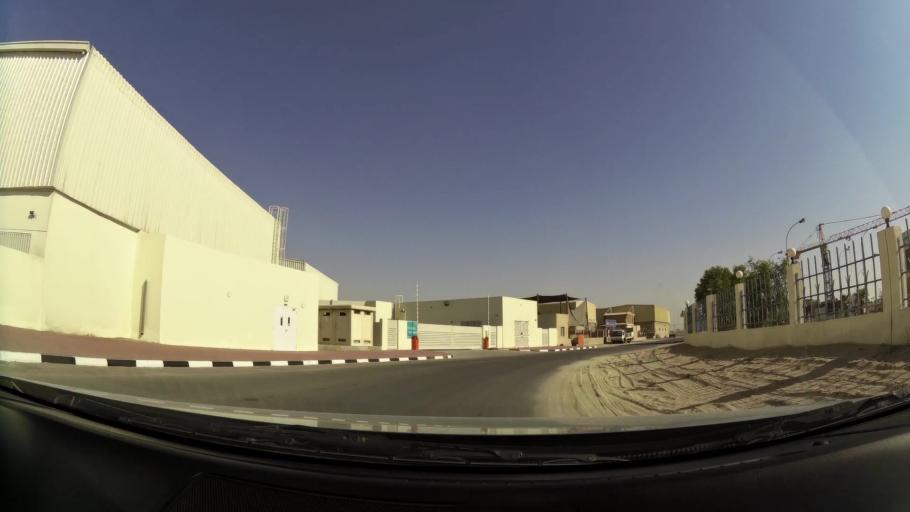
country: AE
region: Dubai
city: Dubai
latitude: 24.9858
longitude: 55.1148
